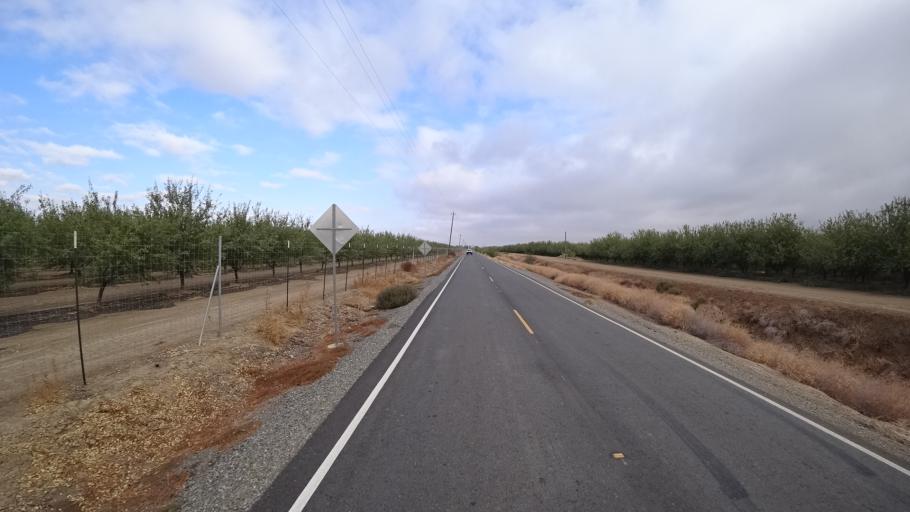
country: US
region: California
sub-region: Yolo County
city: Esparto
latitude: 38.7609
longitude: -122.0442
